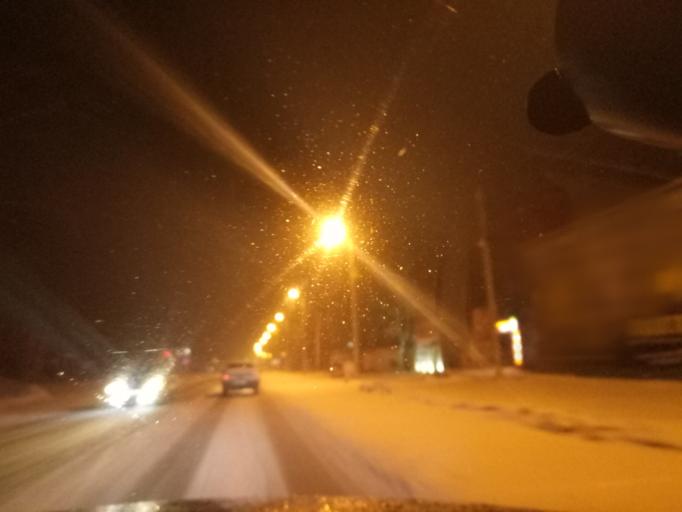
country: RU
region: Tula
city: Novomoskovsk
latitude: 53.9915
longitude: 38.2980
